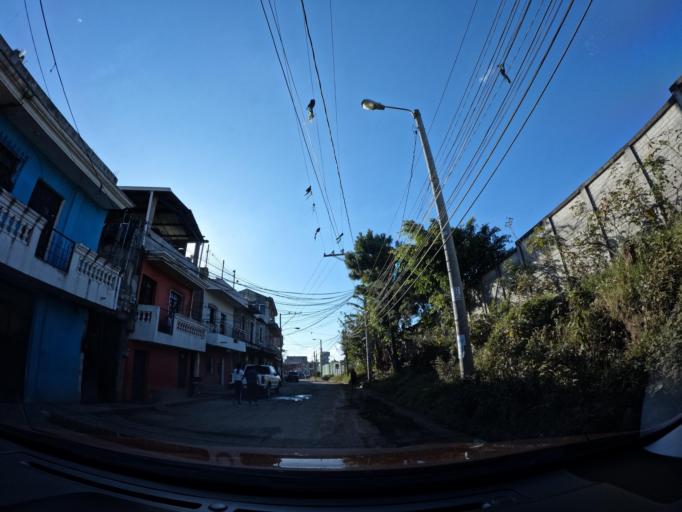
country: GT
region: Escuintla
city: Palin
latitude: 14.4077
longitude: -90.6956
